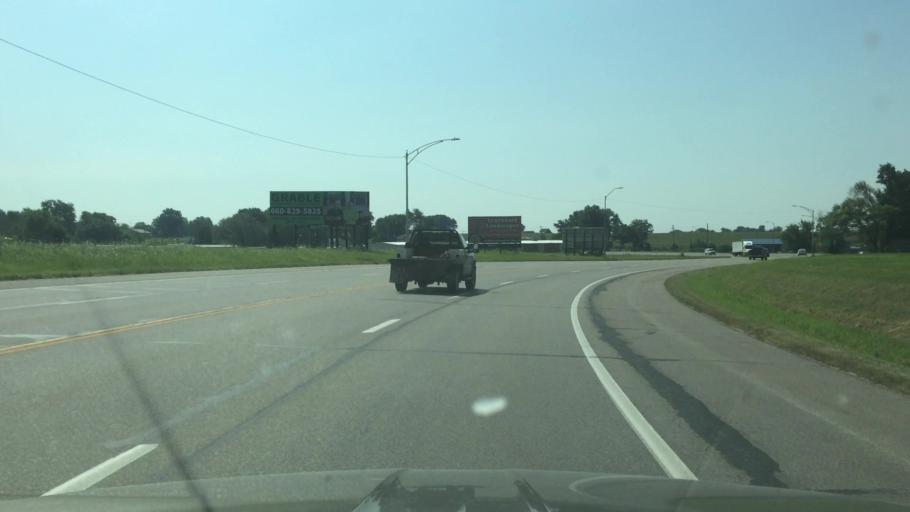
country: US
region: Missouri
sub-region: Pettis County
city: Sedalia
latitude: 38.7025
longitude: -93.1935
